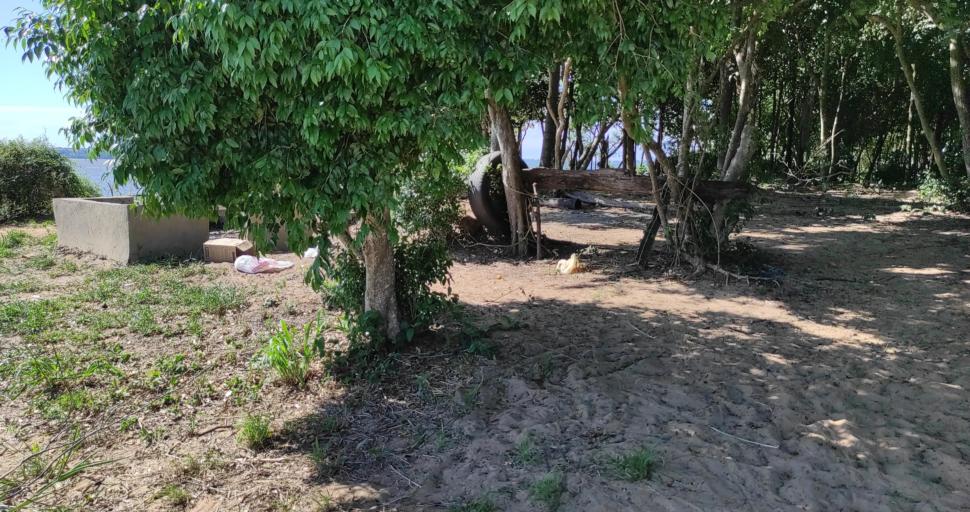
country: PY
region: Itapua
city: San Juan del Parana
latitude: -27.3405
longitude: -55.9509
